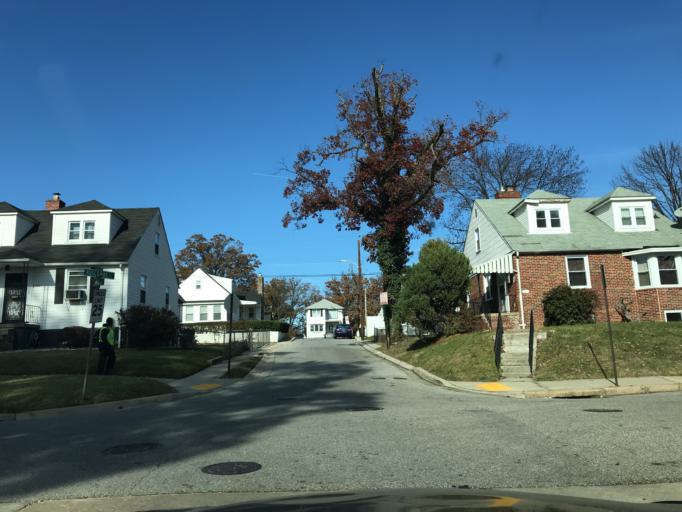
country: US
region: Maryland
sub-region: Baltimore County
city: Lochearn
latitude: 39.3480
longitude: -76.6633
